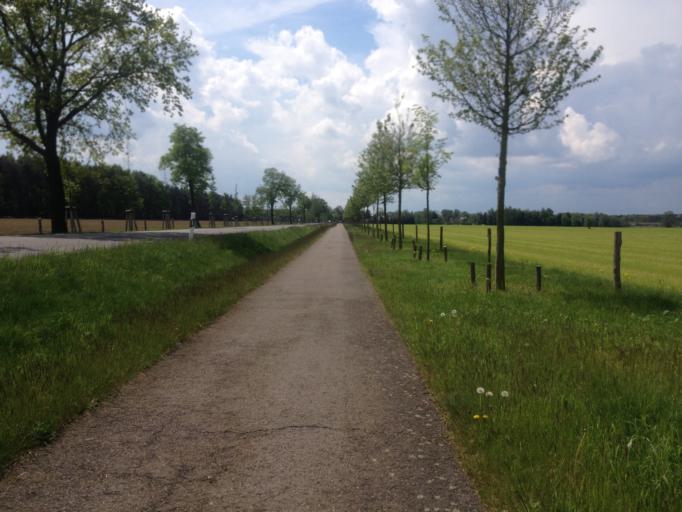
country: DE
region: Brandenburg
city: Briesen
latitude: 51.8258
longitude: 14.2541
